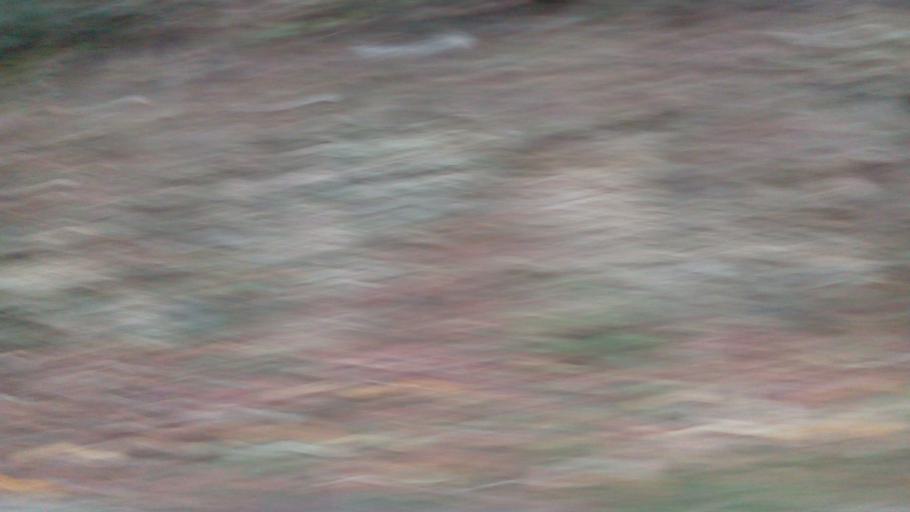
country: TW
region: Taiwan
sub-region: Hualien
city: Hualian
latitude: 24.3580
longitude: 121.3254
